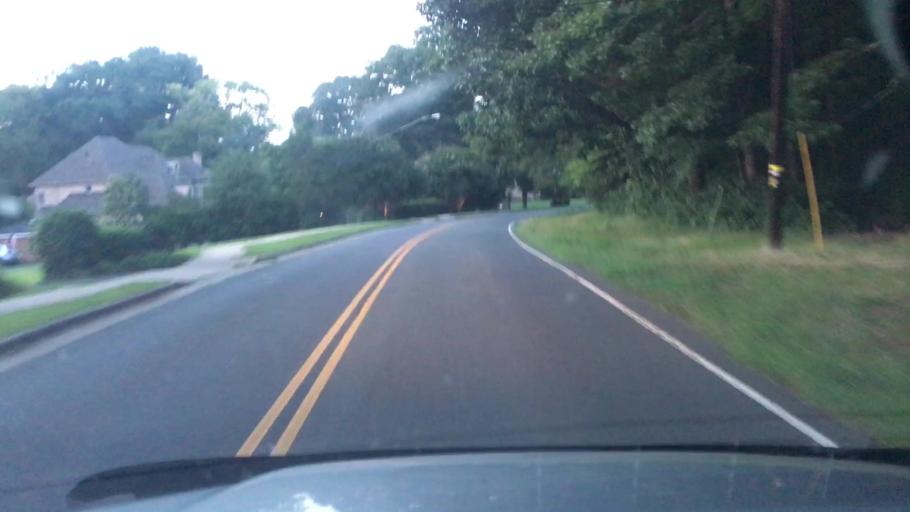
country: US
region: North Carolina
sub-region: Mecklenburg County
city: Matthews
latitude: 35.1362
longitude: -80.8056
